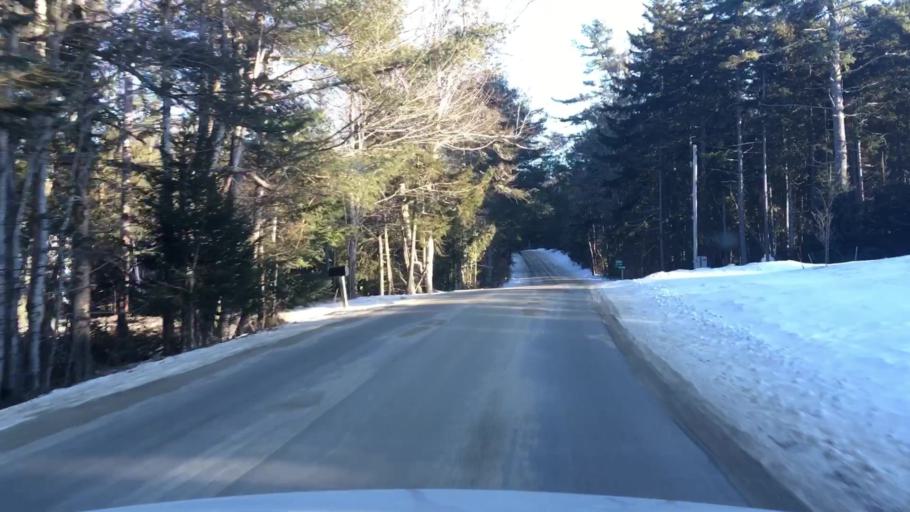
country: US
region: Maine
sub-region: Hancock County
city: Castine
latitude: 44.3836
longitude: -68.7341
